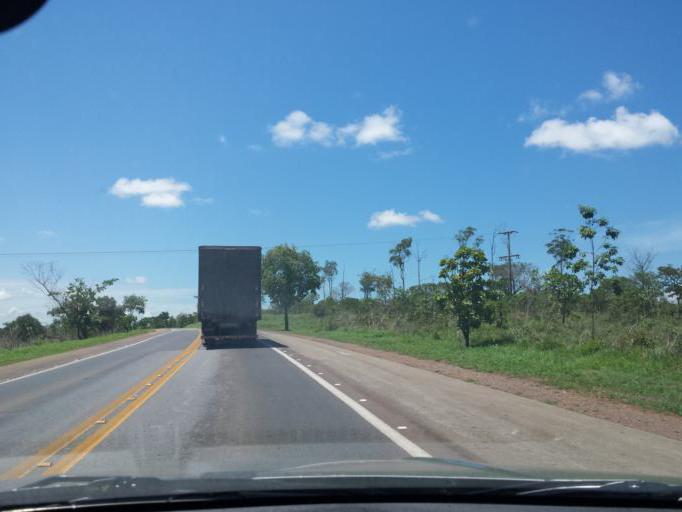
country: BR
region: Goias
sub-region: Luziania
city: Luziania
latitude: -16.5147
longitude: -47.8107
